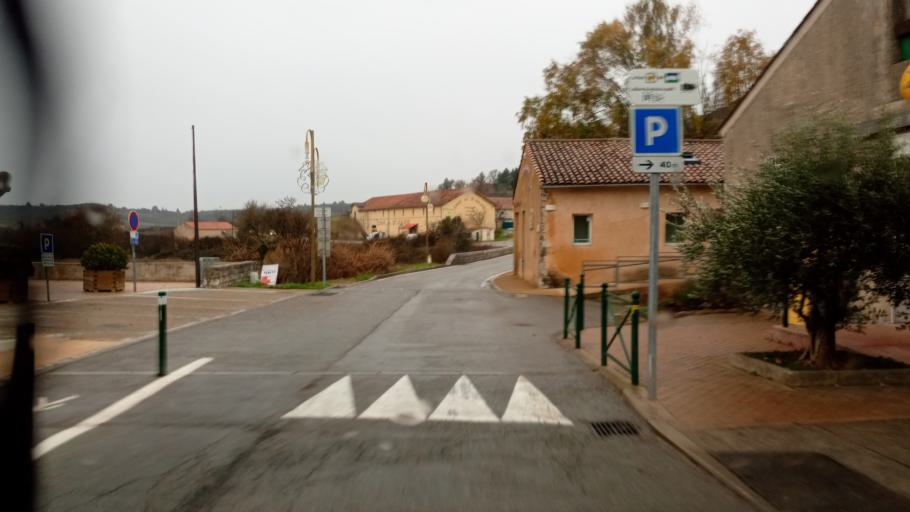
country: FR
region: Provence-Alpes-Cote d'Azur
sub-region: Departement du Var
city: Saint-Julien
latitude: 43.6939
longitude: 5.9150
